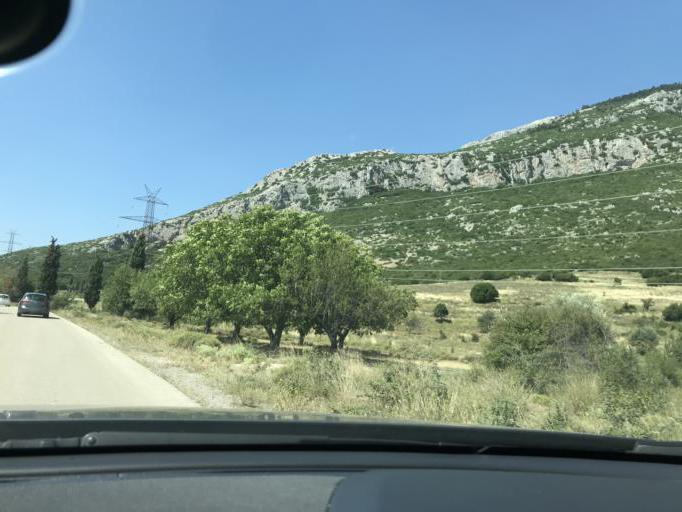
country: GR
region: Central Greece
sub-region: Nomos Voiotias
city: Distomo
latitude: 38.5058
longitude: 22.7048
